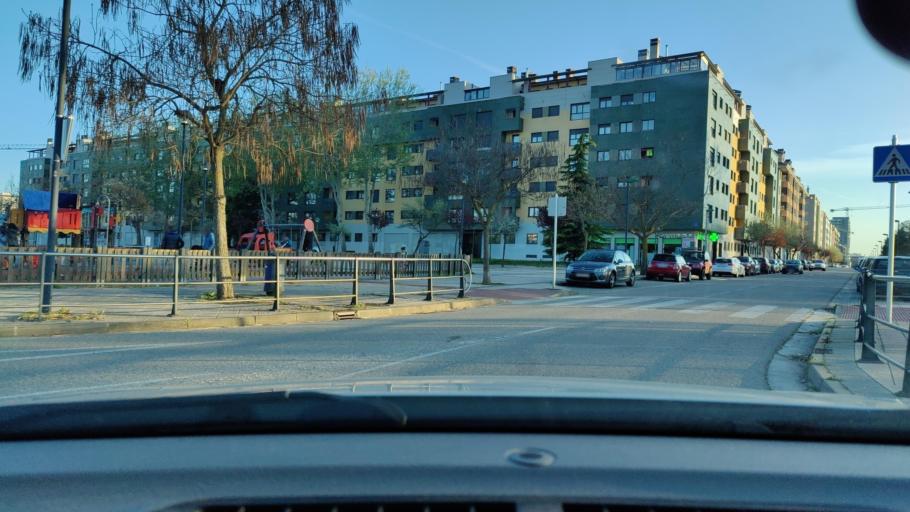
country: ES
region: Castille and Leon
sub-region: Provincia de Burgos
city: Burgos
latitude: 42.3636
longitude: -3.6646
